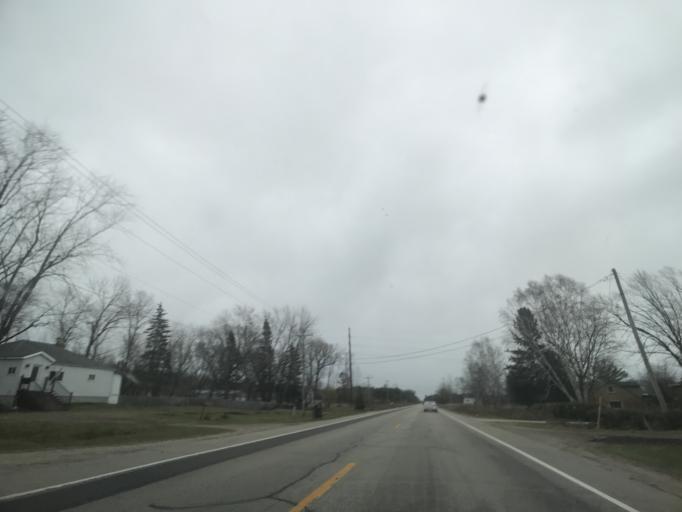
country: US
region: Wisconsin
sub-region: Marinette County
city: Marinette
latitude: 45.0999
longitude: -87.6891
